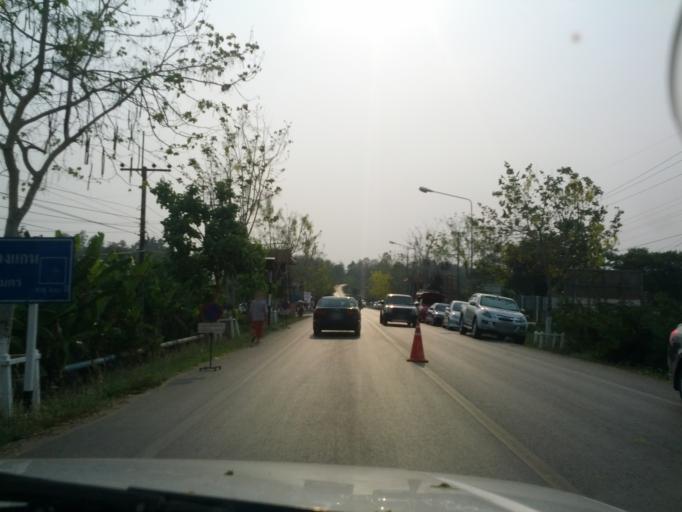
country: TH
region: Chiang Mai
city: Mae Taeng
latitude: 19.1440
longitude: 98.9858
